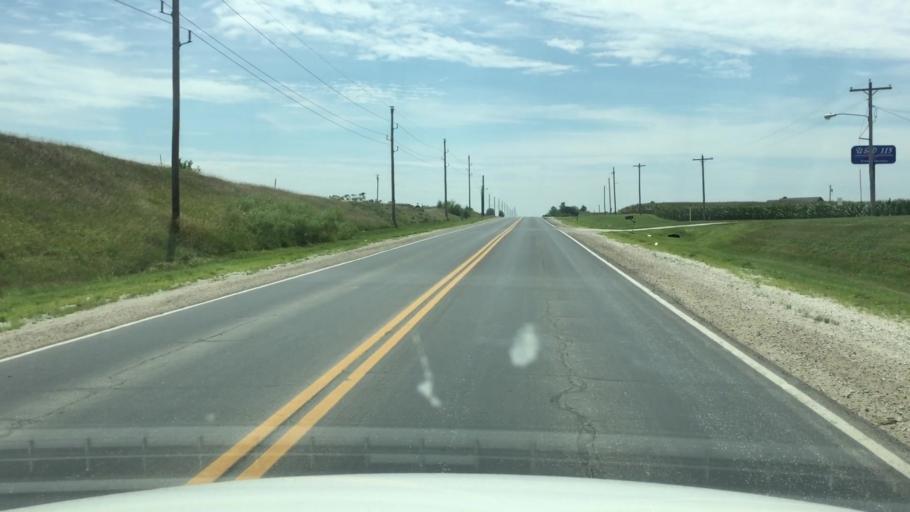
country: US
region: Kansas
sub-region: Nemaha County
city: Sabetha
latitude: 39.8875
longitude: -95.7884
